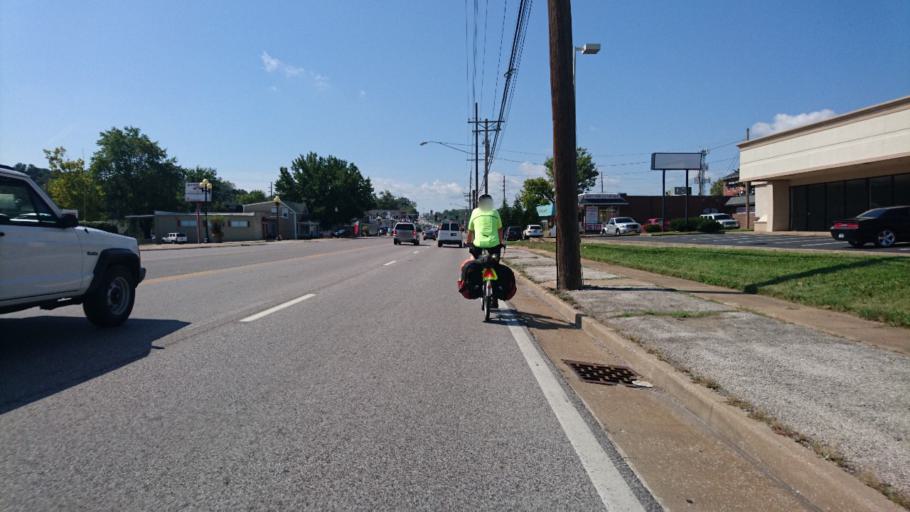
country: US
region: Missouri
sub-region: Saint Louis County
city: Manchester
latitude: 38.5931
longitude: -90.5141
